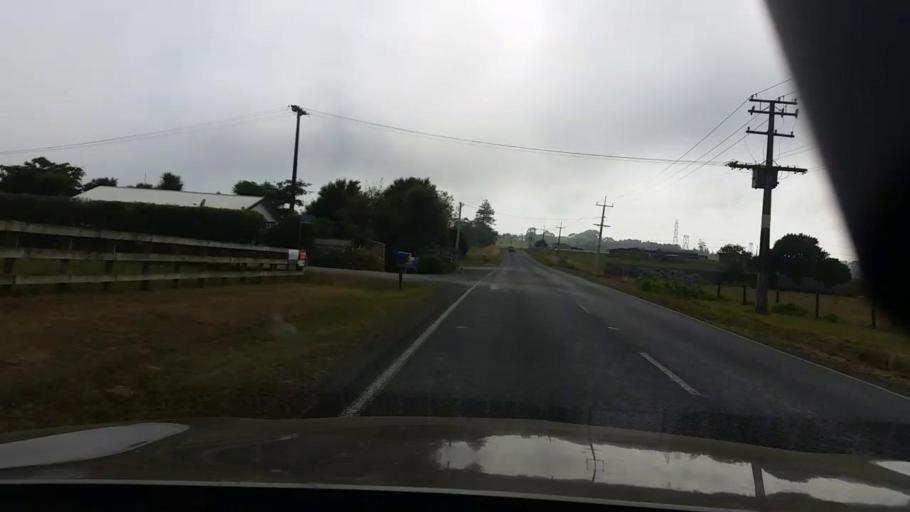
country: NZ
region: Waikato
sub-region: Hamilton City
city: Hamilton
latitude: -37.6209
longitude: 175.3330
